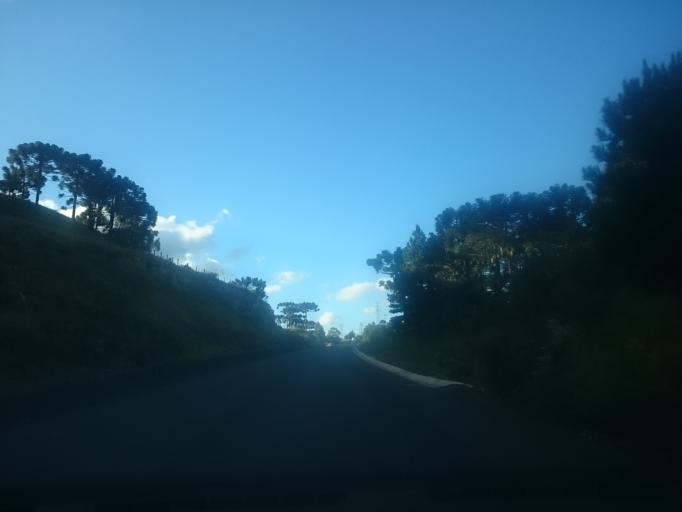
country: BR
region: Santa Catarina
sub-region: Sao Joaquim
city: Sao Joaquim
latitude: -28.0616
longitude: -50.0735
